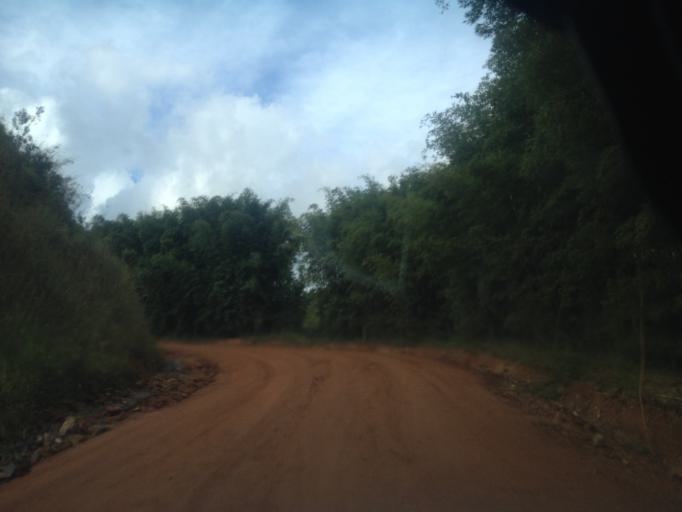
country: BR
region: Rio de Janeiro
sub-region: Quatis
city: Quatis
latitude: -22.2148
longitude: -44.2458
